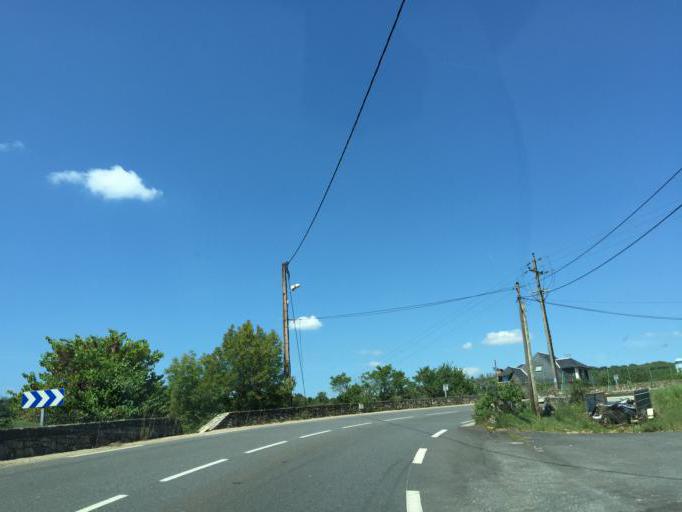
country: FR
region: Midi-Pyrenees
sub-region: Departement de l'Aveyron
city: Espalion
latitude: 44.5295
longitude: 2.7619
